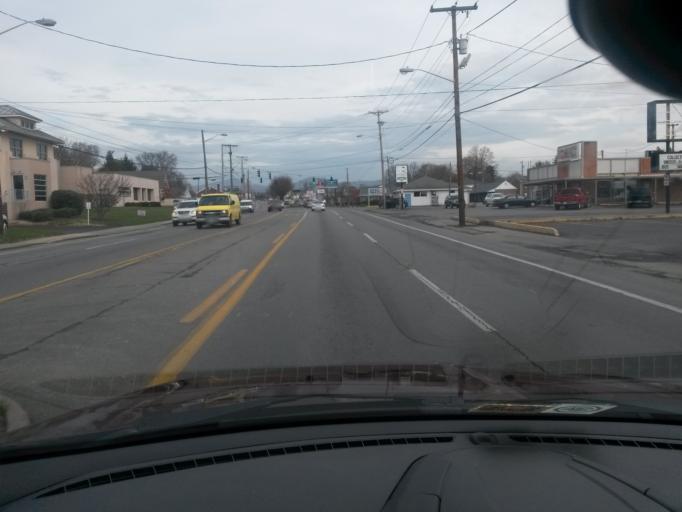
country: US
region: Virginia
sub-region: Roanoke County
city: Hollins
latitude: 37.3119
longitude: -79.9510
